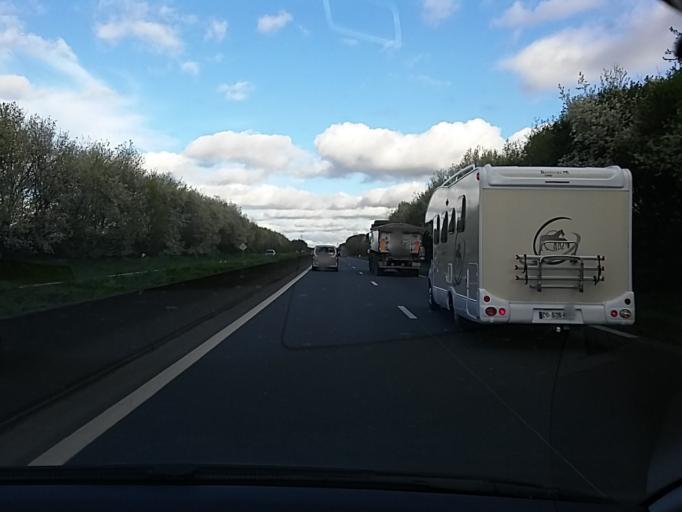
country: FR
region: Picardie
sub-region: Departement de la Somme
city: Camon
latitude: 49.9047
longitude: 2.3519
